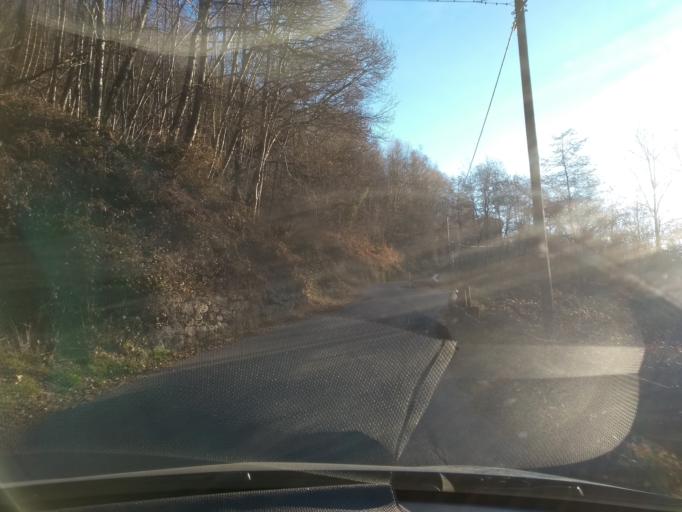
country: IT
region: Piedmont
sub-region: Provincia di Torino
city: Corio
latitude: 45.3213
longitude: 7.5294
